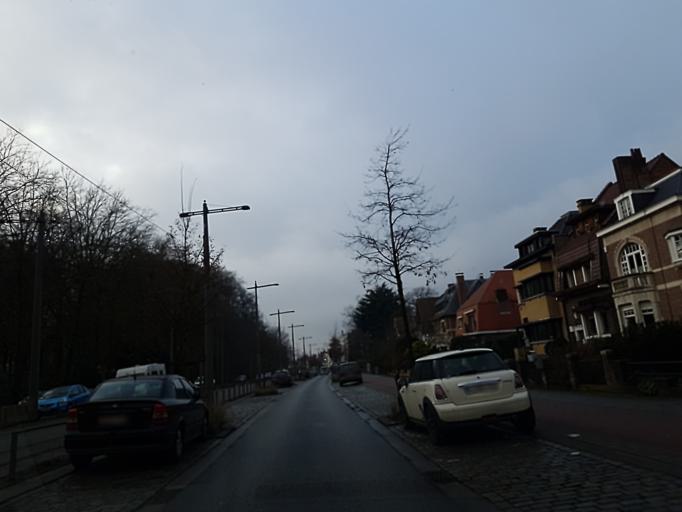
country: BE
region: Flanders
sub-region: Provincie Antwerpen
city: Borsbeek
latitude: 51.2193
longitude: 4.4729
